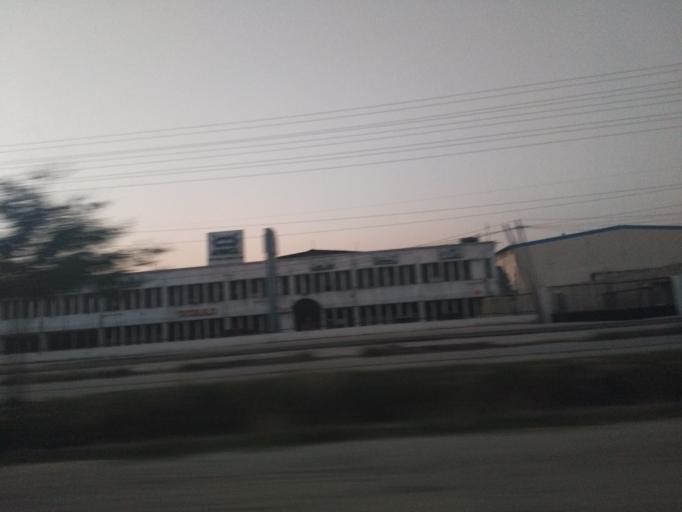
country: TZ
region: Dar es Salaam
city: Dar es Salaam
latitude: -6.8534
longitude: 39.2266
